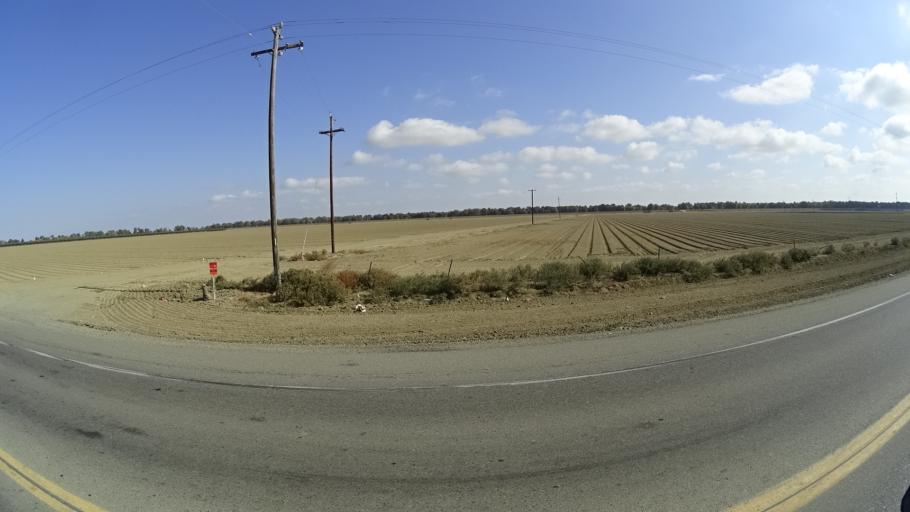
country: US
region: California
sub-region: Yolo County
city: Woodland
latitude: 38.7150
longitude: -121.7300
